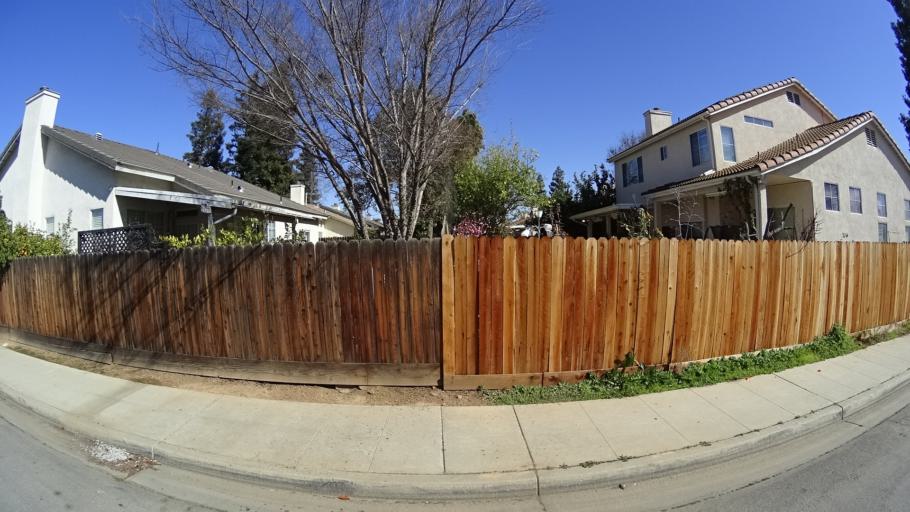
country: US
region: California
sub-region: Fresno County
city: Clovis
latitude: 36.8609
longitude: -119.7429
